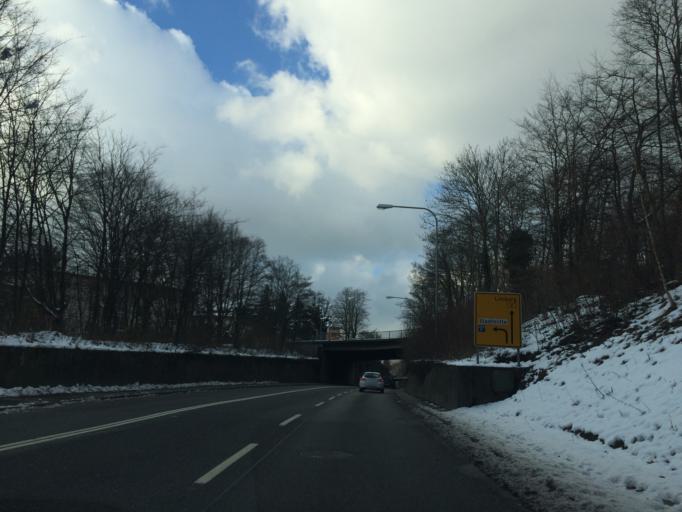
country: DE
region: Hesse
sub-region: Regierungsbezirk Darmstadt
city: Konigstein im Taunus
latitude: 50.1815
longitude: 8.4735
